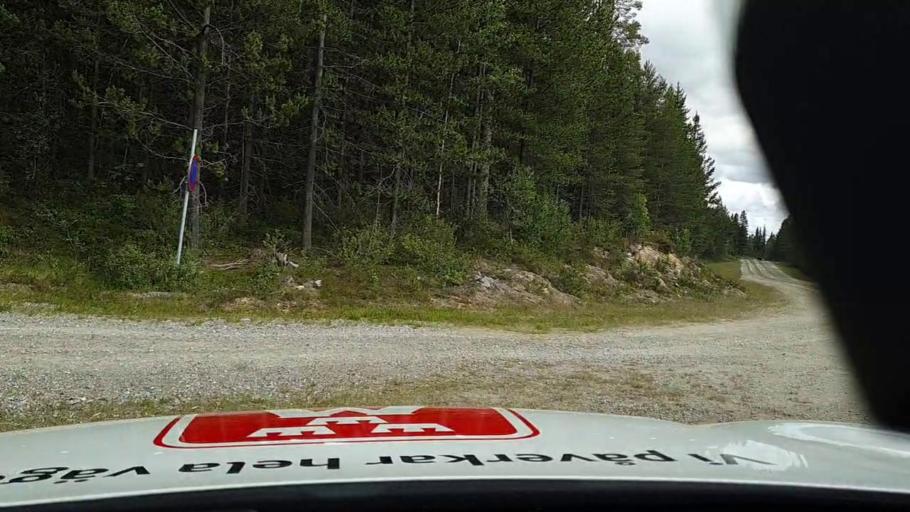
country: SE
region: Jaemtland
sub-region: Are Kommun
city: Jarpen
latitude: 62.5787
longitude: 13.3905
